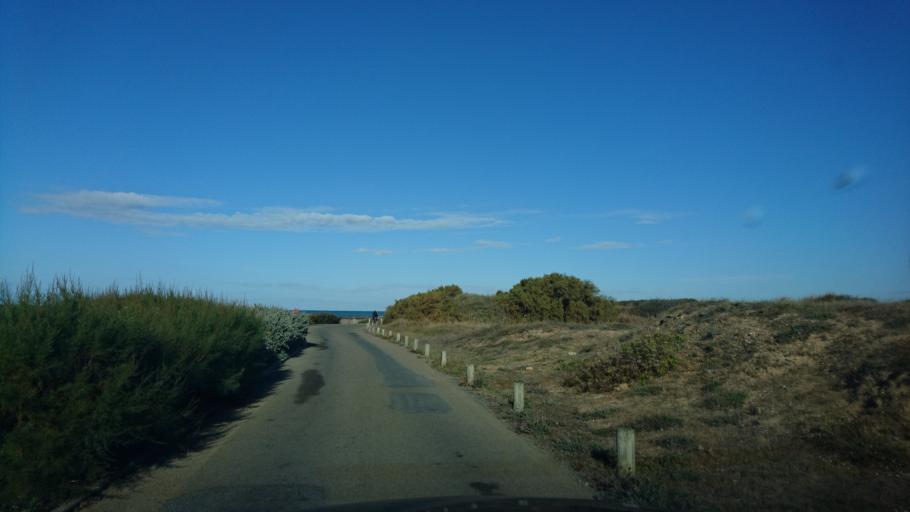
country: FR
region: Pays de la Loire
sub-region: Departement de la Vendee
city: Les Sables-d'Olonne
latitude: 46.5058
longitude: -1.8164
